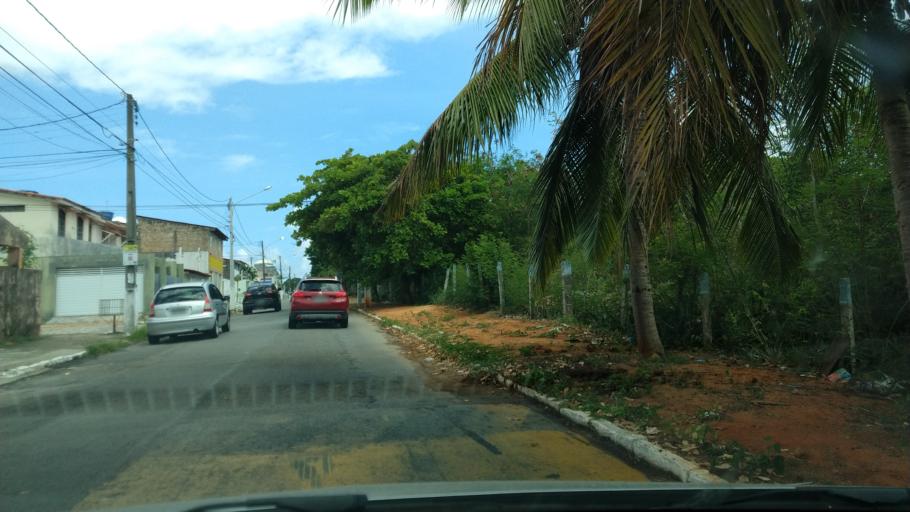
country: BR
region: Rio Grande do Norte
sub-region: Natal
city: Natal
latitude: -5.8526
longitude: -35.1993
